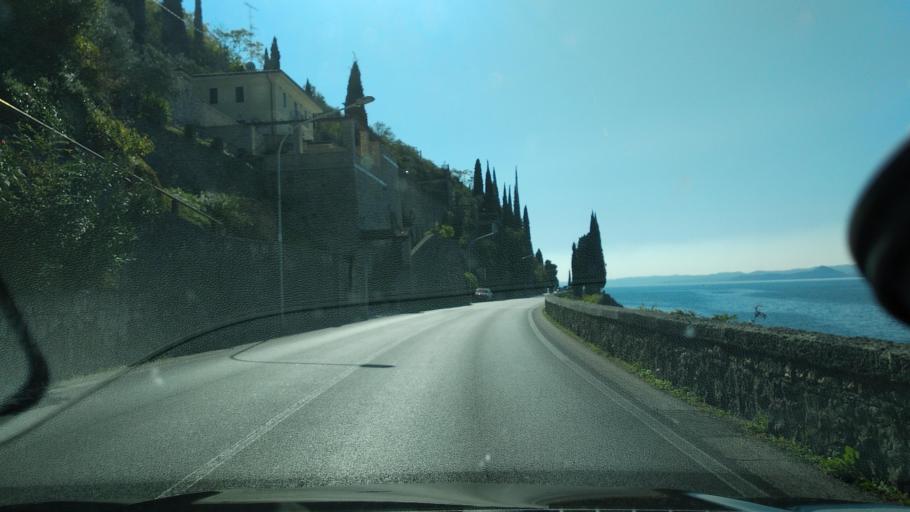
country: IT
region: Veneto
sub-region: Provincia di Verona
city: Torri del Benaco
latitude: 45.5934
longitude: 10.6825
